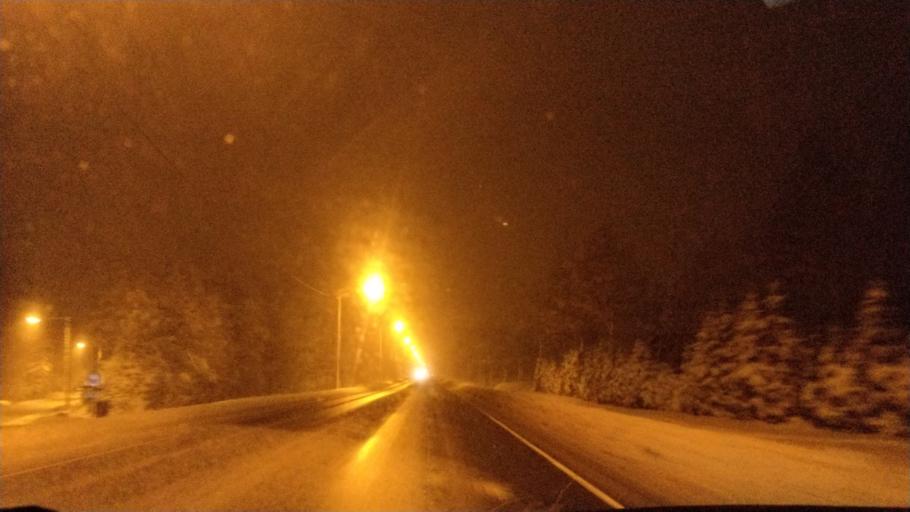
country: FI
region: Lapland
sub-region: Rovaniemi
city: Rovaniemi
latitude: 66.4759
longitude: 25.6224
